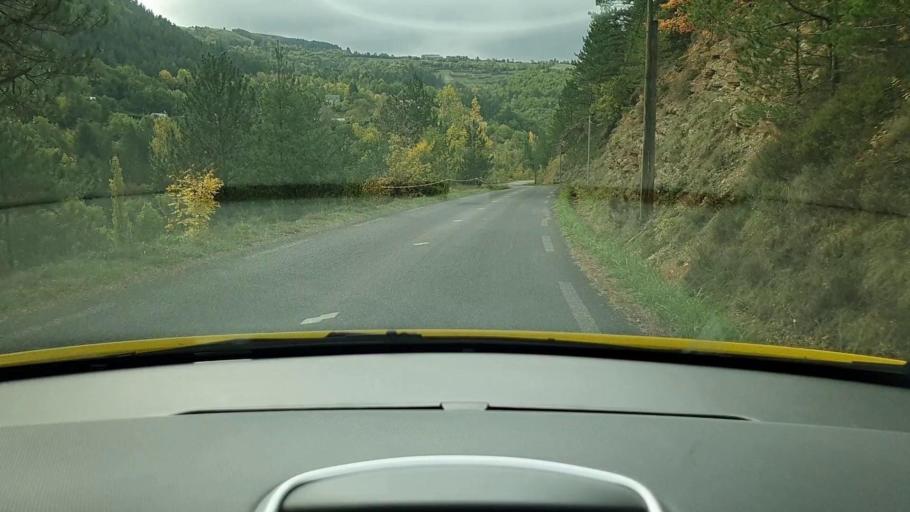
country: FR
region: Languedoc-Roussillon
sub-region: Departement de la Lozere
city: Meyrueis
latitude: 44.0832
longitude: 3.3939
